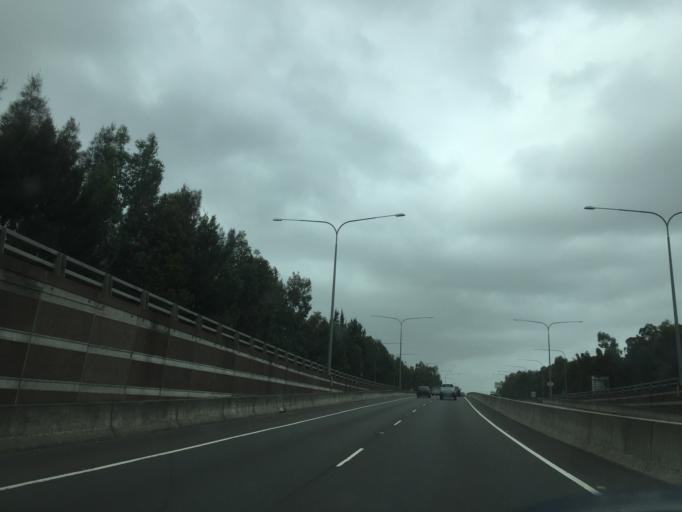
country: AU
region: New South Wales
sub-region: Blacktown
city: Stanhope Gardens
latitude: -33.7417
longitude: 150.9477
